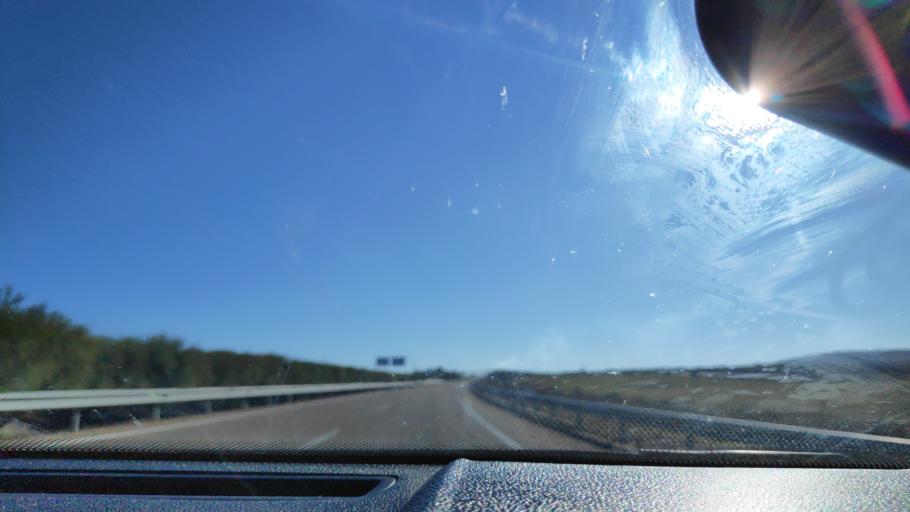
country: ES
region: Extremadura
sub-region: Provincia de Badajoz
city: Villafranca de los Barros
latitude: 38.5229
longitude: -6.3498
